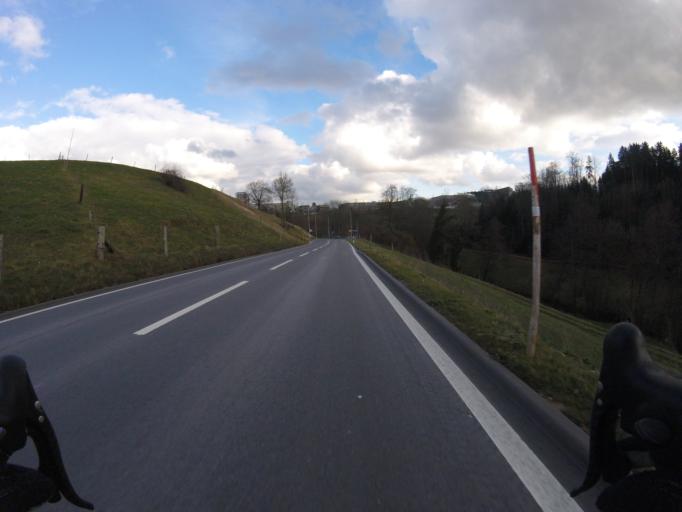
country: CH
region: Bern
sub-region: Bern-Mittelland District
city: Wohlen
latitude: 46.9475
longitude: 7.3686
